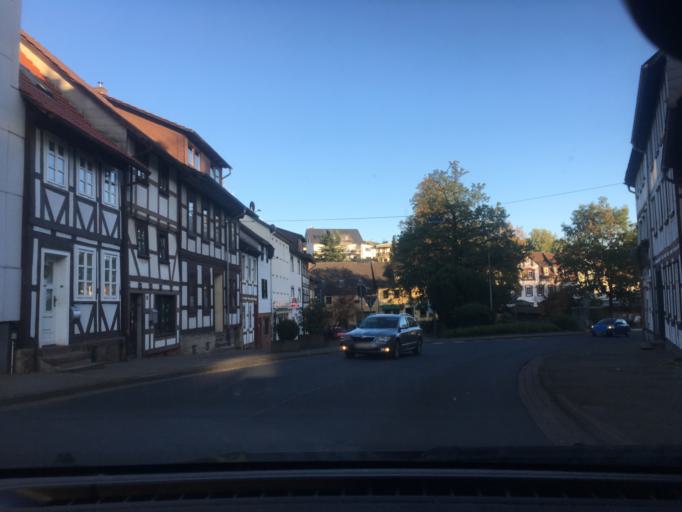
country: DE
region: Lower Saxony
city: Uslar
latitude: 51.6606
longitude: 9.6388
